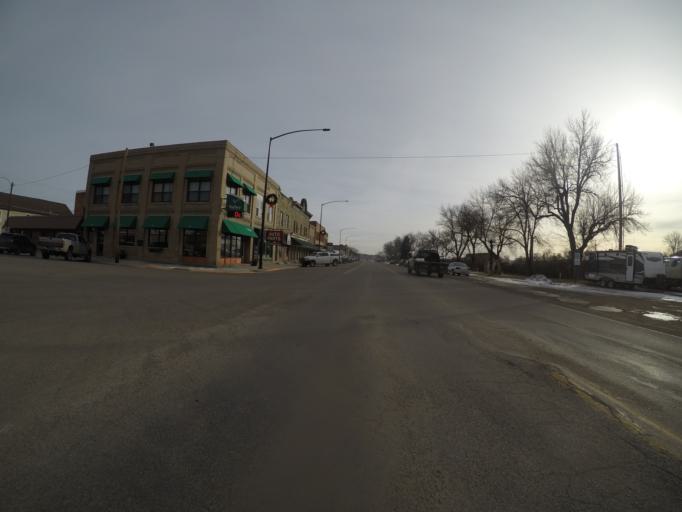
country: US
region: Montana
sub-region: Stillwater County
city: Columbus
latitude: 45.6375
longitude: -109.2552
